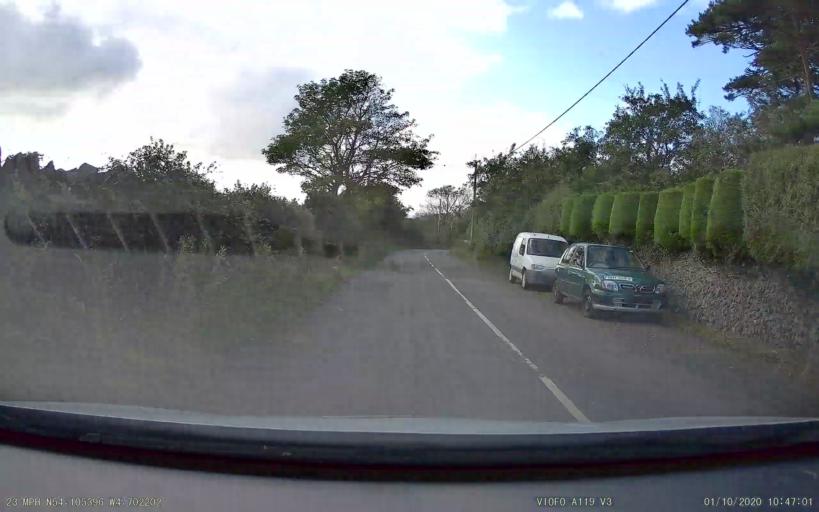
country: IM
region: Port Erin
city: Port Erin
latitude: 54.1054
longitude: -4.7022
